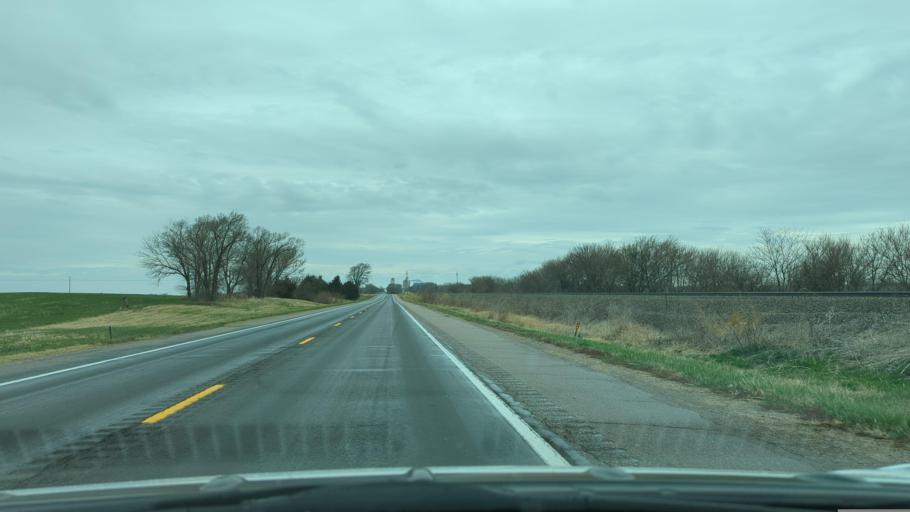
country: US
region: Nebraska
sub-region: Saunders County
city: Ashland
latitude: 40.9791
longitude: -96.4250
